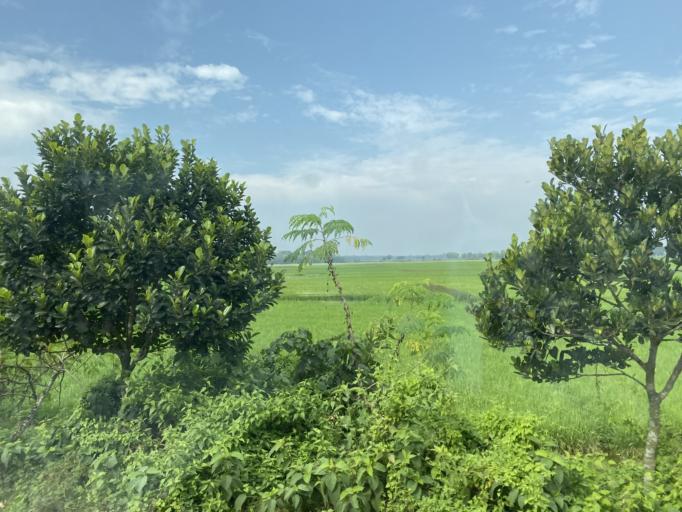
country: IN
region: Tripura
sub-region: West Tripura
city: Agartala
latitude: 23.9901
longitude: 91.2848
